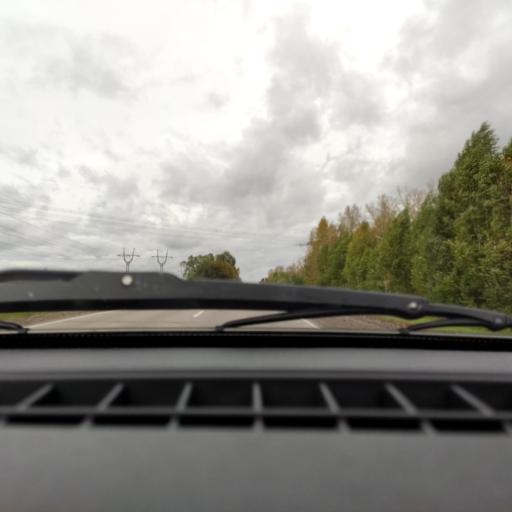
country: RU
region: Bashkortostan
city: Chishmy
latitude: 54.5161
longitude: 55.2951
